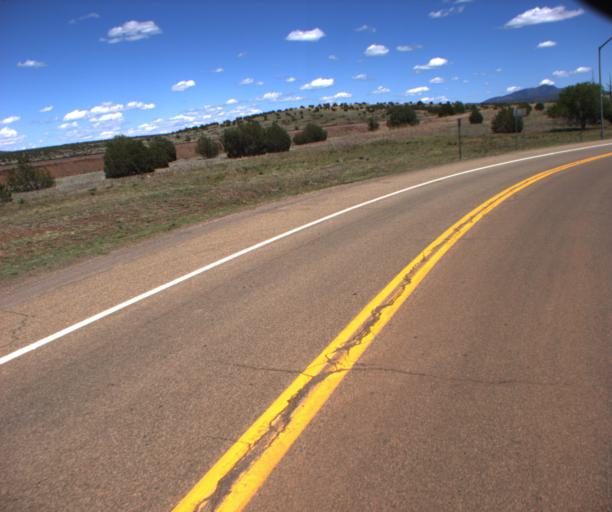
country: US
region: Arizona
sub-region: Coconino County
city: Williams
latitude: 35.2227
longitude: -112.4753
